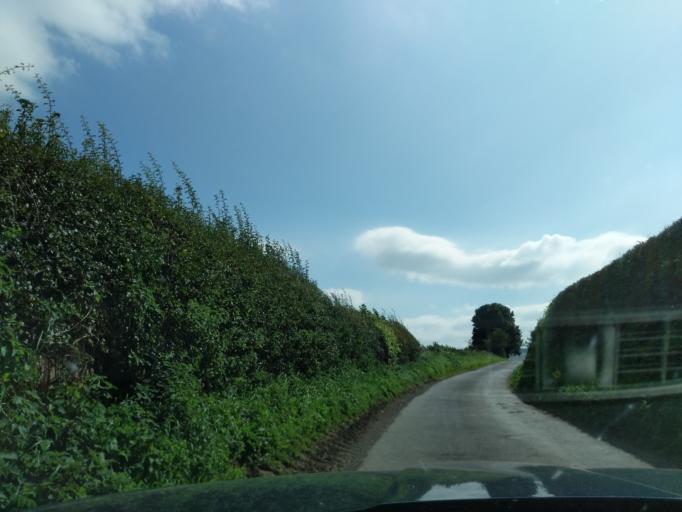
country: GB
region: England
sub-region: Northumberland
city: Ford
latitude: 55.6455
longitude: -2.1377
